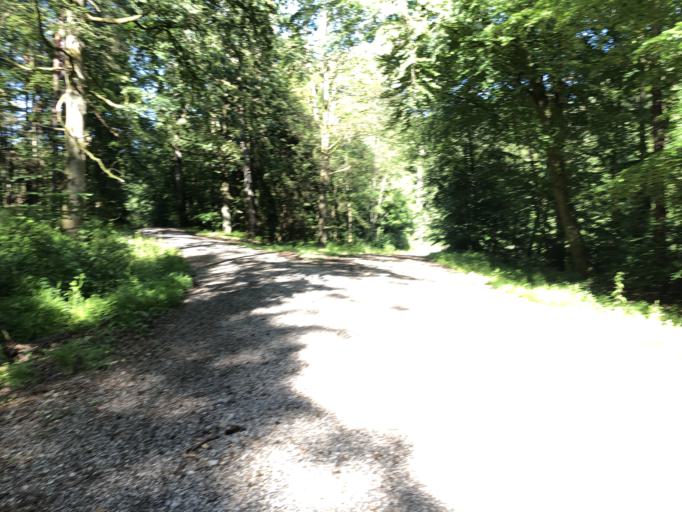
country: DE
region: Bavaria
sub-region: Upper Franconia
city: Memmelsdorf
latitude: 49.9136
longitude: 10.9720
